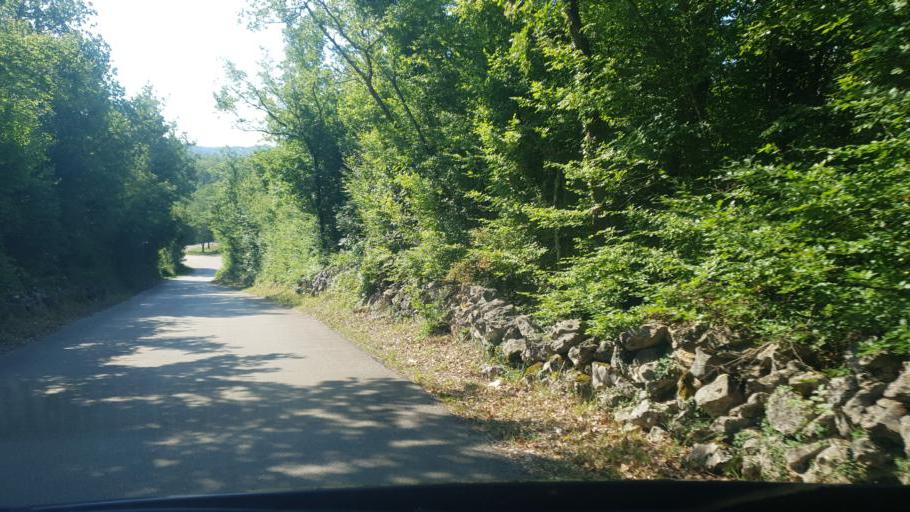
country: HR
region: Primorsko-Goranska
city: Njivice
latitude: 45.1444
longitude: 14.5815
